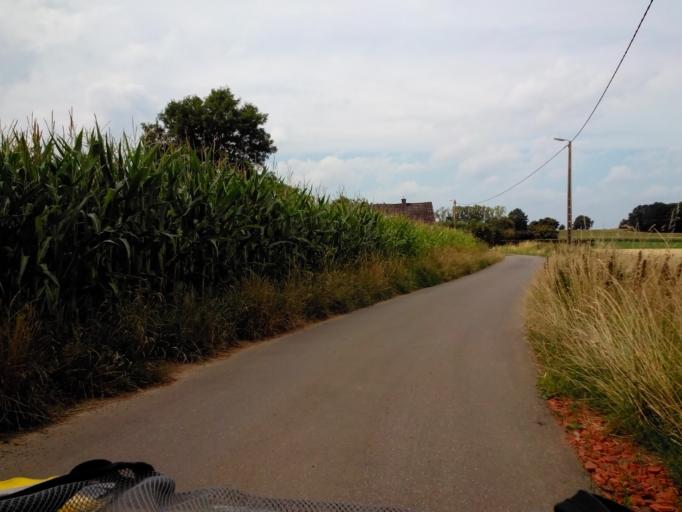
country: BE
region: Flanders
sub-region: Provincie Vlaams-Brabant
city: Holsbeek
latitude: 50.9034
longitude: 4.7888
